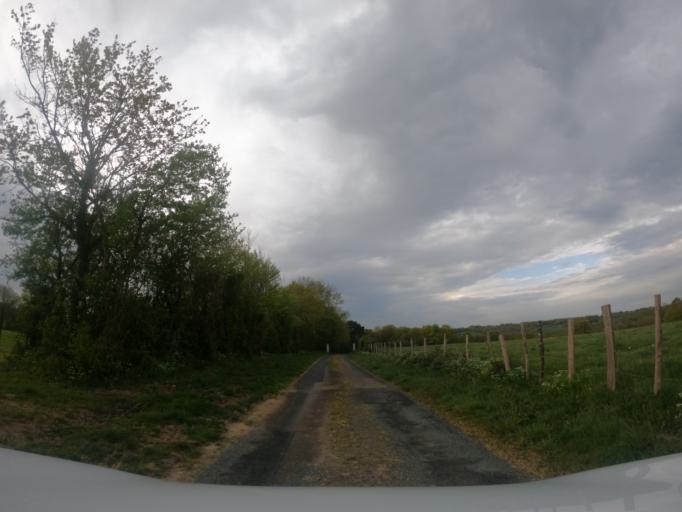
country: FR
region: Pays de la Loire
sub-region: Departement de la Vendee
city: Le Champ-Saint-Pere
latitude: 46.5114
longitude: -1.3583
